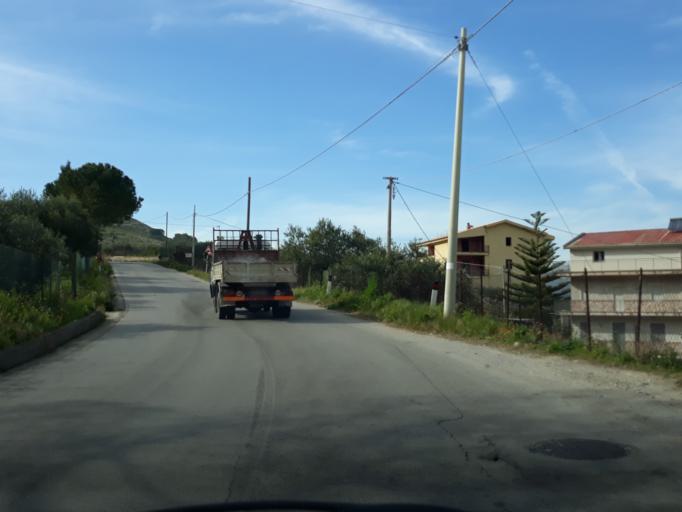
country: IT
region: Sicily
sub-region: Palermo
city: Piano Maglio-Blandino
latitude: 38.0404
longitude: 13.3176
